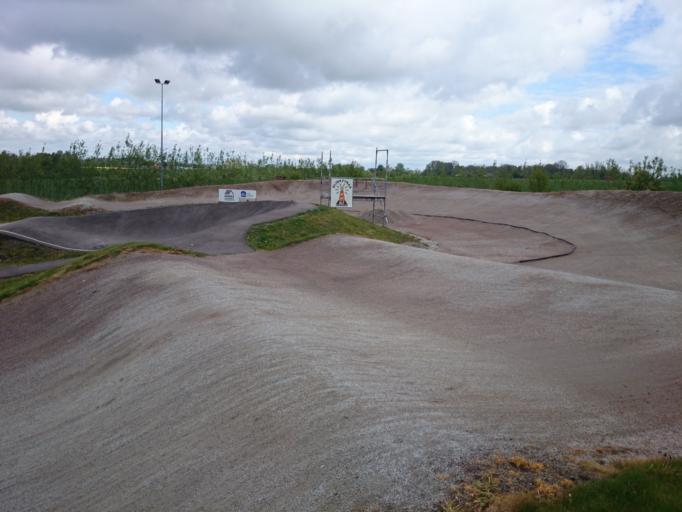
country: SE
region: Skane
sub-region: Malmo
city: Oxie
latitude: 55.5711
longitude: 13.0875
